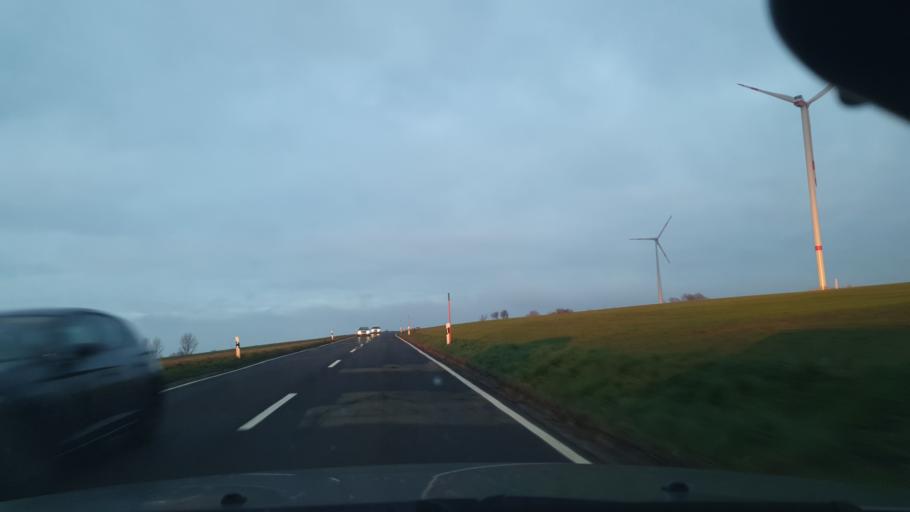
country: DE
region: Rheinland-Pfalz
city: Langwieden
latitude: 49.3724
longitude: 7.5081
